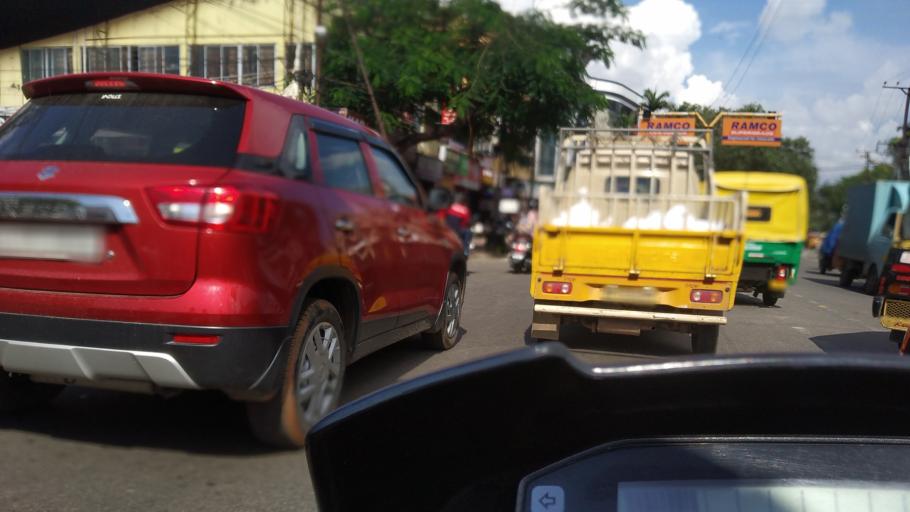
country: IN
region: Kerala
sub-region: Ernakulam
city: Cochin
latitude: 9.9850
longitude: 76.2769
